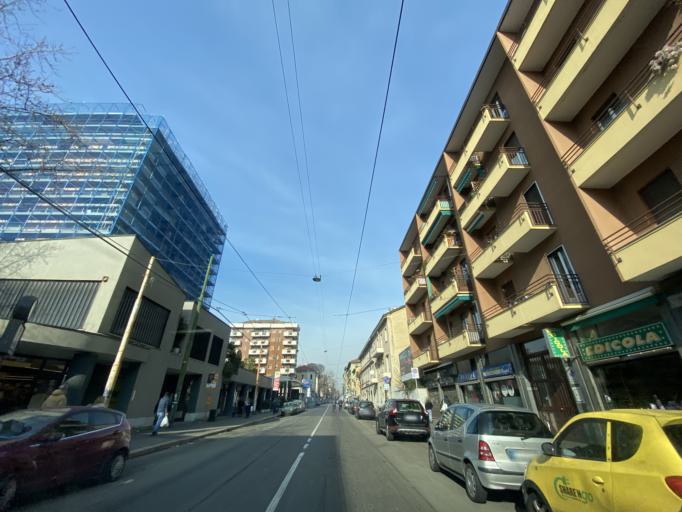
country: IT
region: Lombardy
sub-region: Citta metropolitana di Milano
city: Bresso
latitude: 45.5149
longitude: 9.1730
